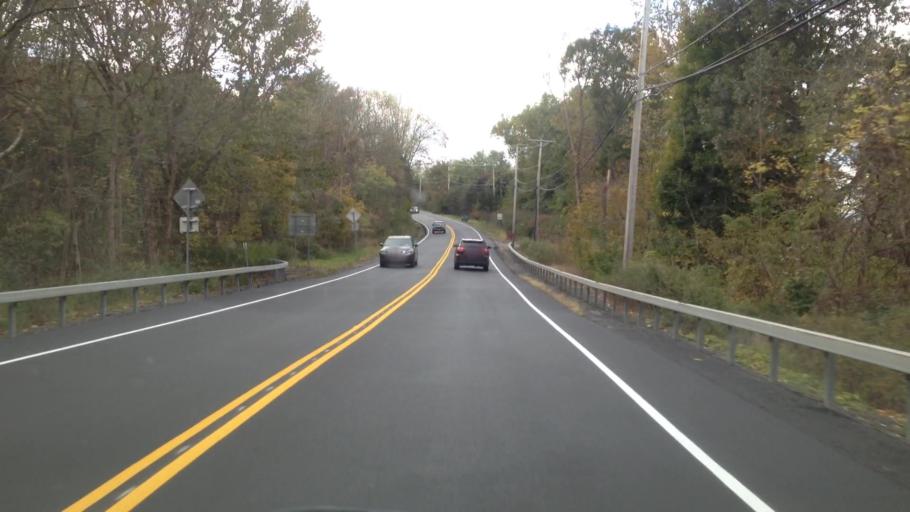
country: US
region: New York
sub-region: Ulster County
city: New Paltz
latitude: 41.7250
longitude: -74.1050
